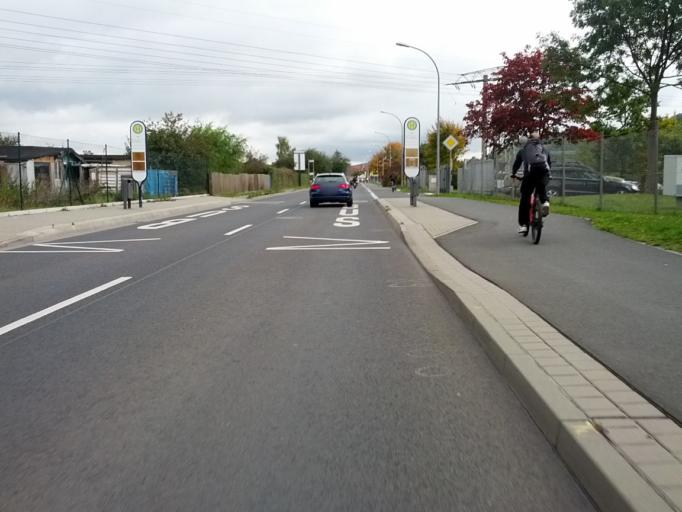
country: DE
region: Thuringia
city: Eisenach
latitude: 50.9802
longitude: 10.2889
